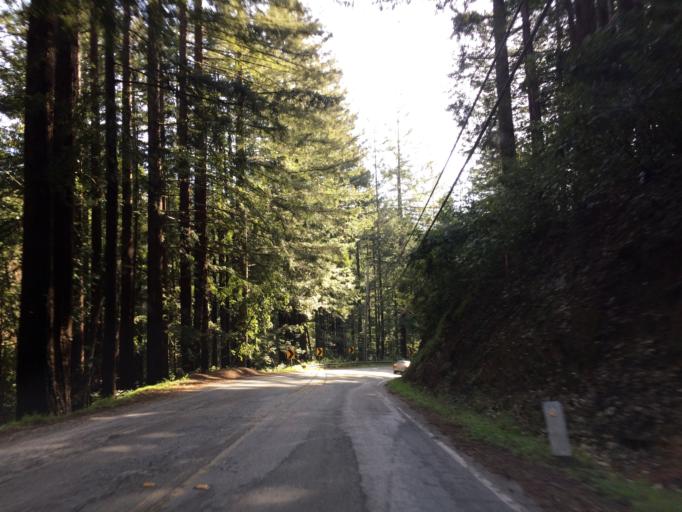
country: US
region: California
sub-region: Santa Cruz County
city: Pasatiempo
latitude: 37.0014
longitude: -122.0709
